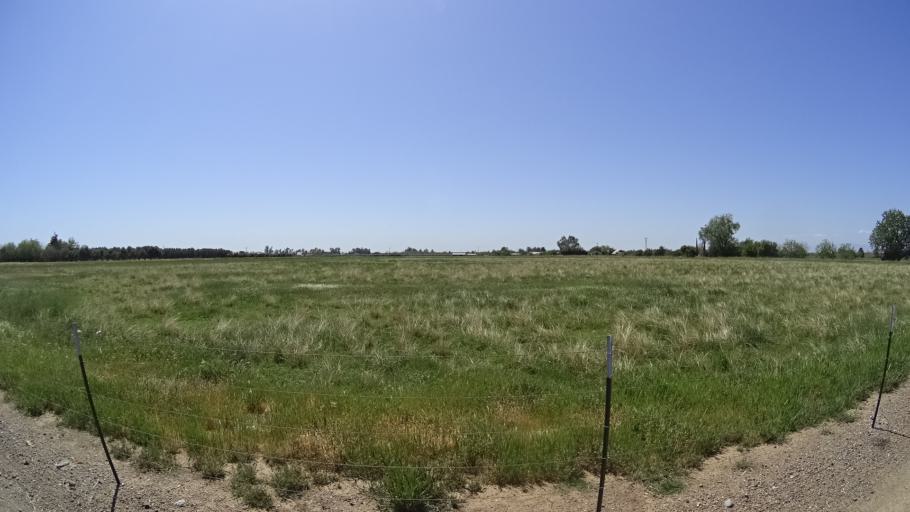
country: US
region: California
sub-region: Glenn County
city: Orland
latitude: 39.7837
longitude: -122.1819
